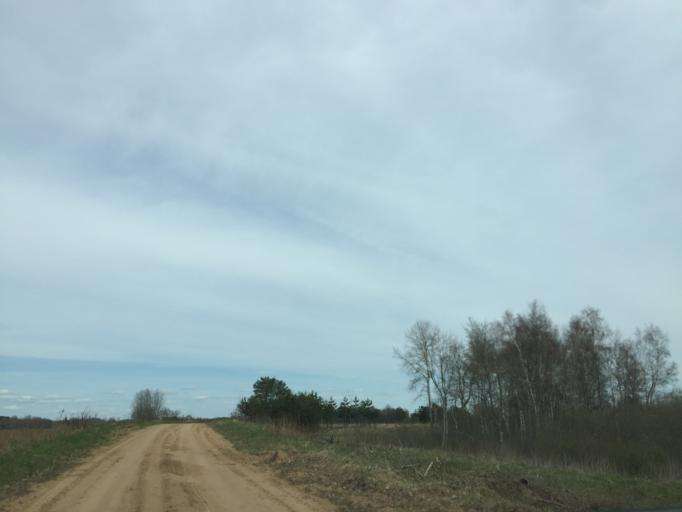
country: LV
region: Ludzas Rajons
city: Ludza
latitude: 56.5147
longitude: 27.5682
